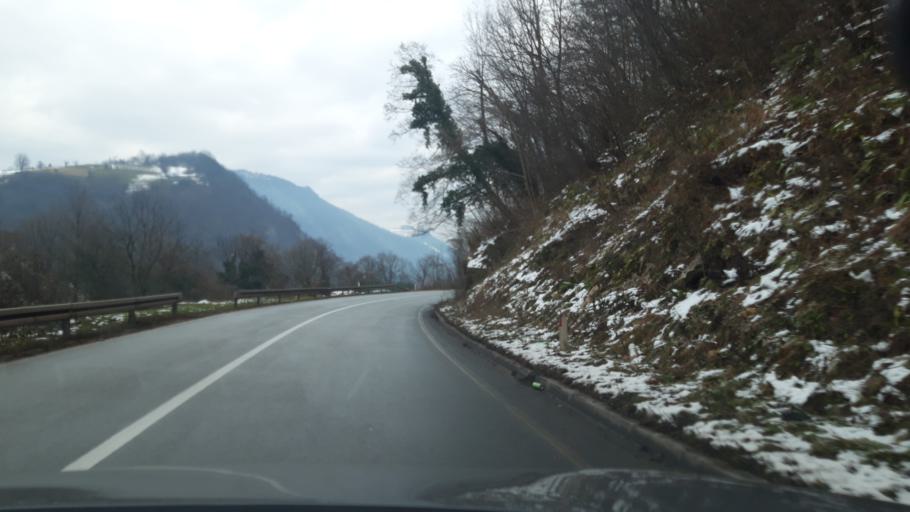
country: RS
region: Central Serbia
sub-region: Macvanski Okrug
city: Mali Zvornik
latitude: 44.3187
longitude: 19.1262
